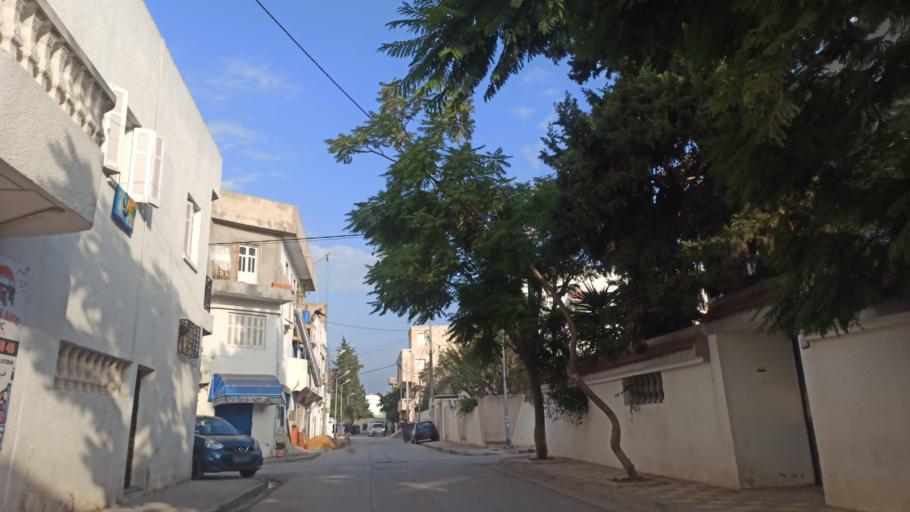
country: TN
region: Tunis
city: La Goulette
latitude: 36.8533
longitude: 10.2647
